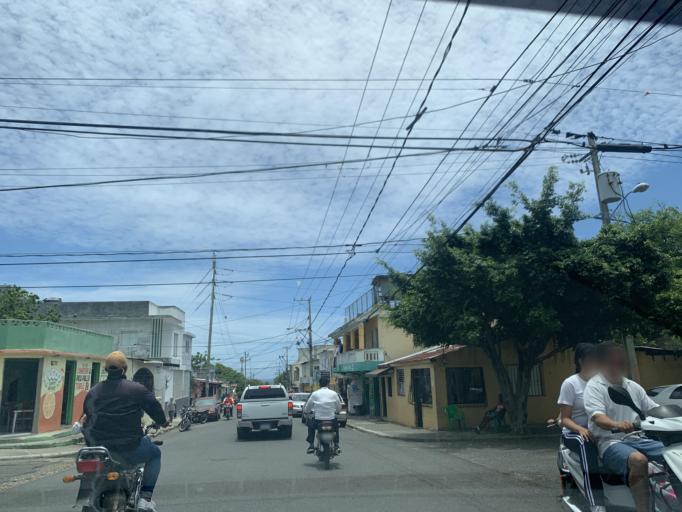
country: DO
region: Puerto Plata
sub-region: Puerto Plata
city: Puerto Plata
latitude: 19.7897
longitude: -70.6855
